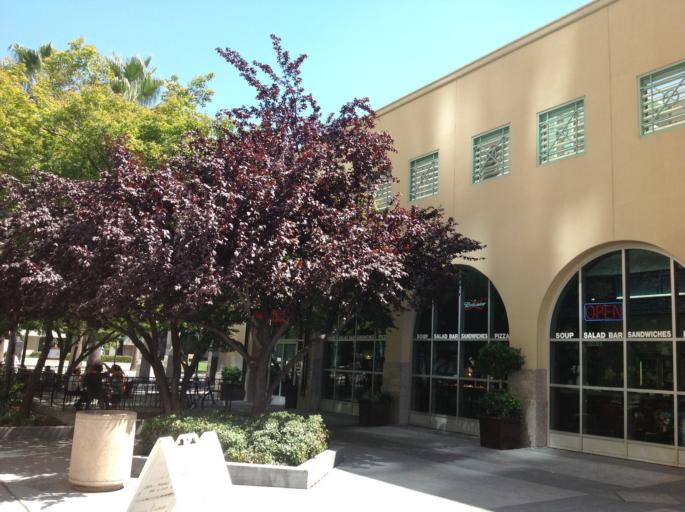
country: US
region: California
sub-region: Sacramento County
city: Sacramento
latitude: 38.5784
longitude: -121.4902
